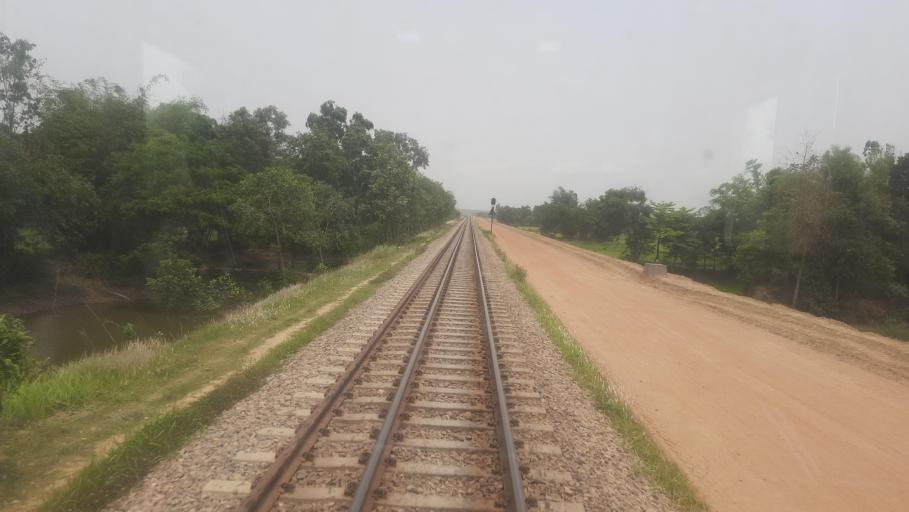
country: BD
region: Chittagong
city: Comilla
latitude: 23.6477
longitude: 91.1476
